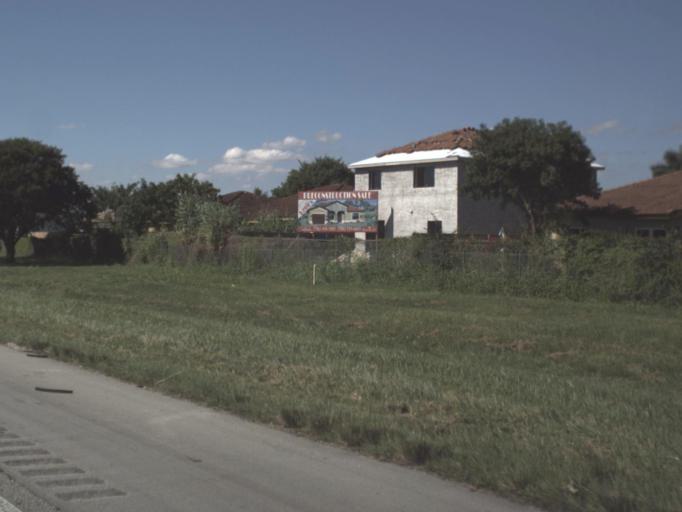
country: US
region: Florida
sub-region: Miami-Dade County
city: Naranja
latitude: 25.5157
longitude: -80.4073
